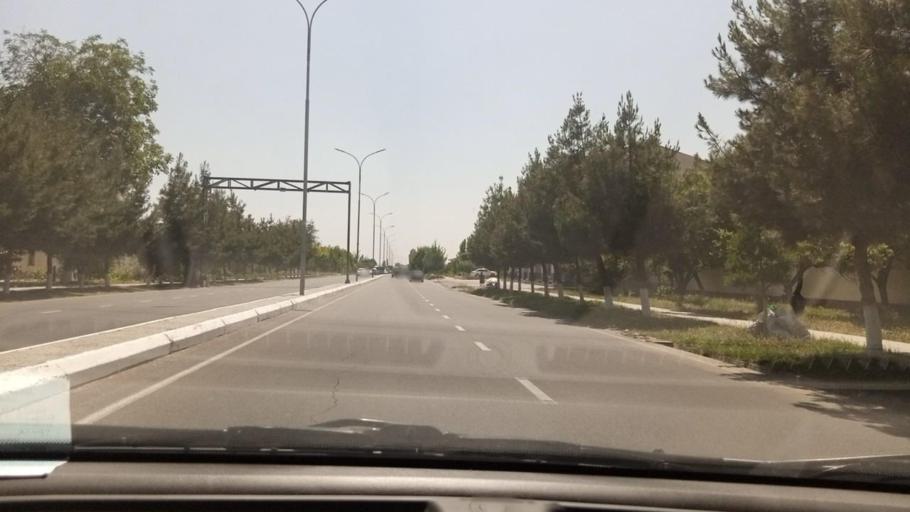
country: UZ
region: Toshkent
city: Urtaowul
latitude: 41.2090
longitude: 69.1697
